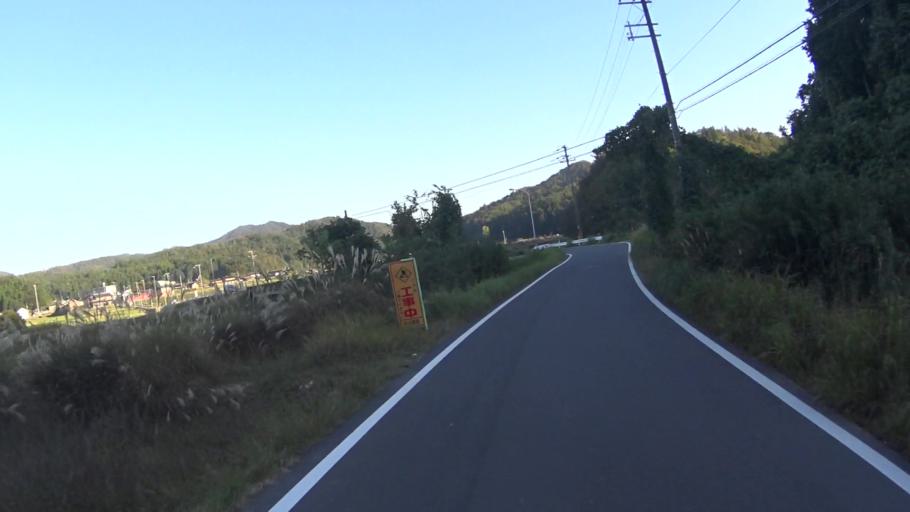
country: JP
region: Hyogo
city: Toyooka
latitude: 35.6215
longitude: 134.9399
